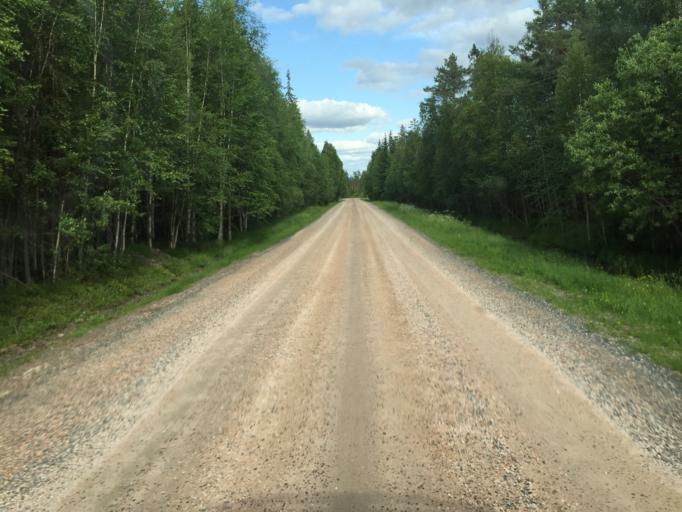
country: SE
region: Dalarna
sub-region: Malung-Saelens kommun
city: Malung
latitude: 60.9416
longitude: 13.8729
